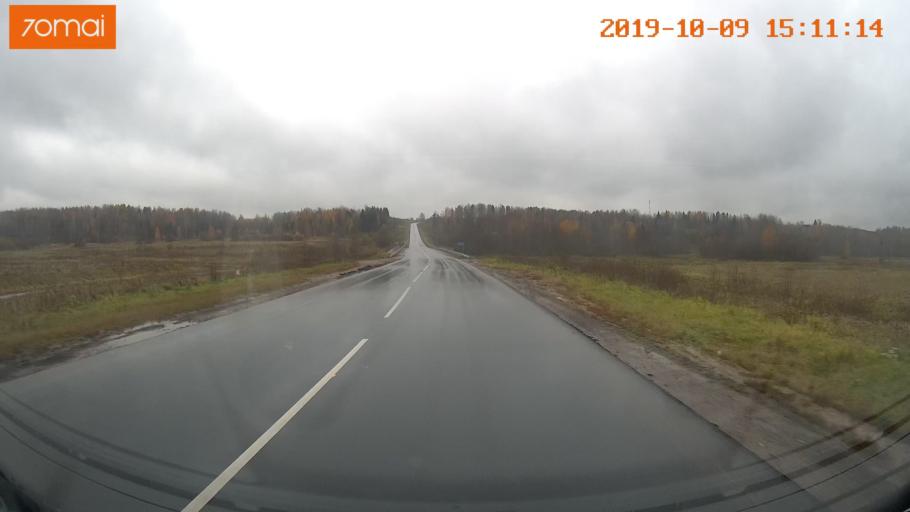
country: RU
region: Kostroma
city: Susanino
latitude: 58.1678
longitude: 41.6312
